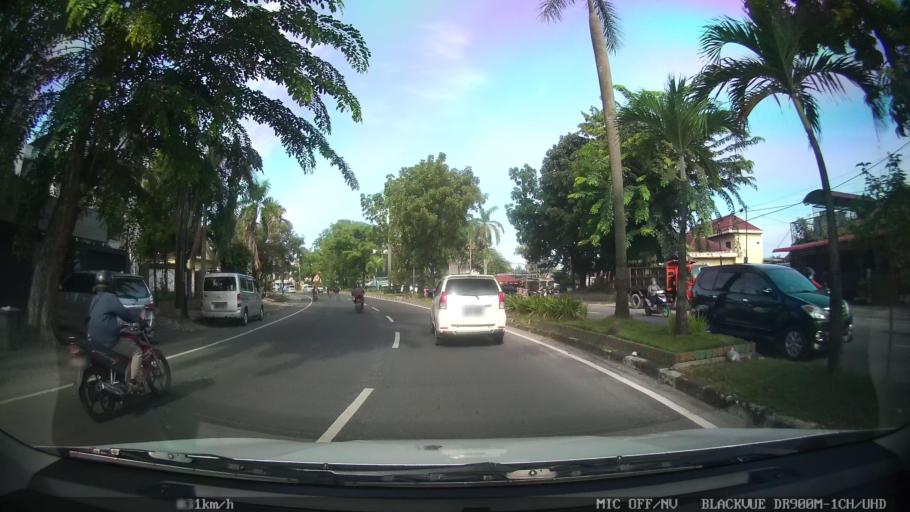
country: ID
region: North Sumatra
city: Medan
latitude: 3.6081
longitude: 98.6477
